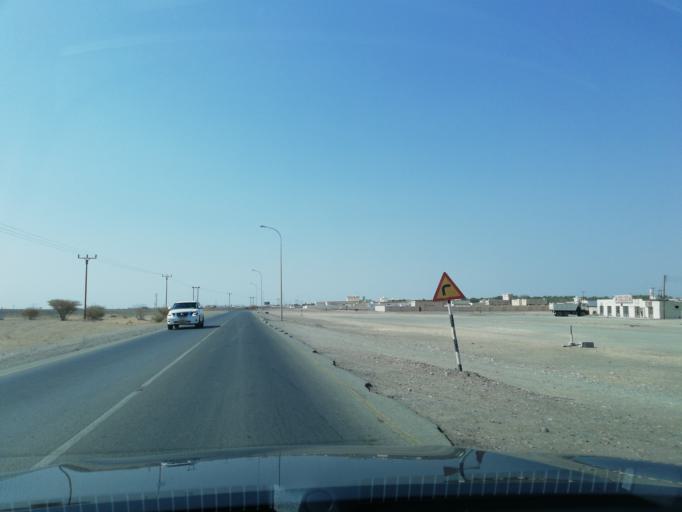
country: OM
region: Muhafazat ad Dakhiliyah
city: Adam
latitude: 22.3083
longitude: 58.0709
